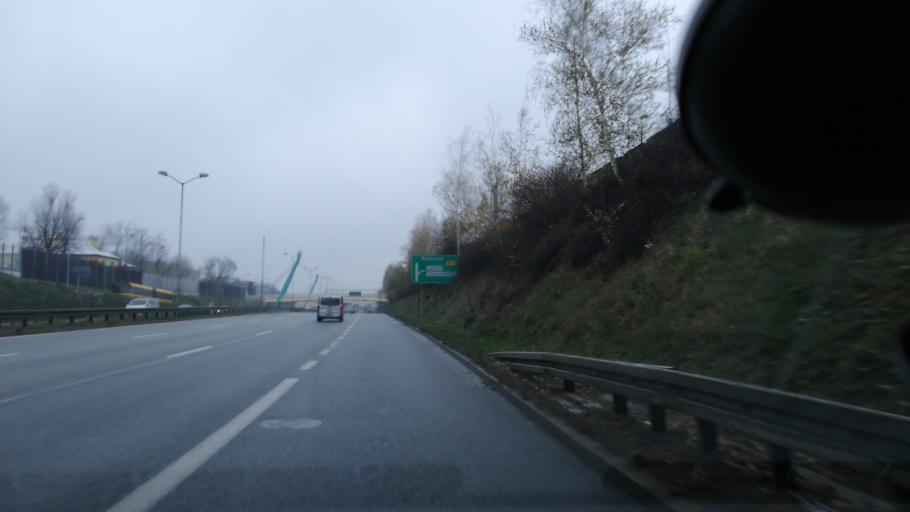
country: PL
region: Silesian Voivodeship
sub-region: Swietochlowice
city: Swietochlowice
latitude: 50.2848
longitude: 18.9417
